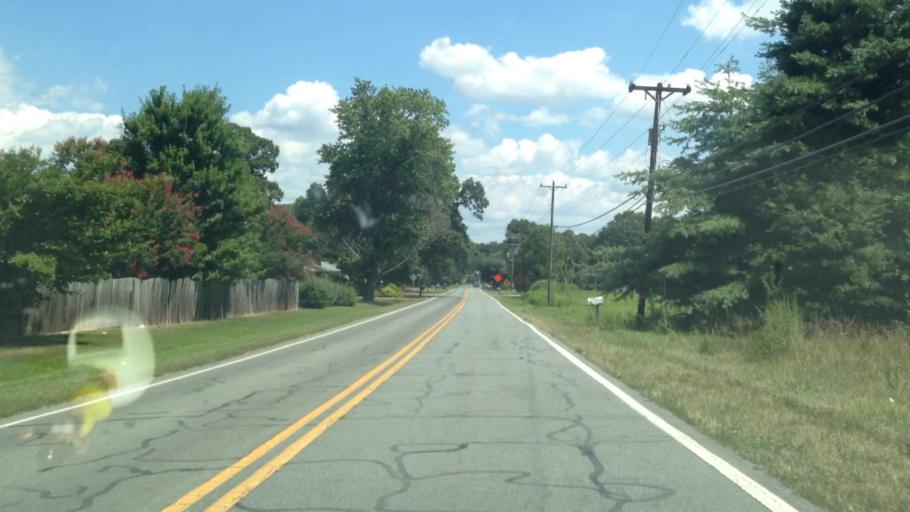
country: US
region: North Carolina
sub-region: Forsyth County
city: Kernersville
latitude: 36.1501
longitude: -80.0628
